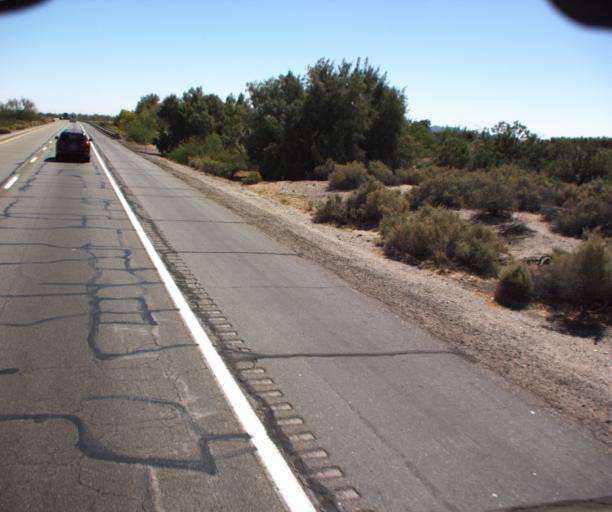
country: US
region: Arizona
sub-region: Yuma County
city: Wellton
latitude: 32.6502
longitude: -114.2159
